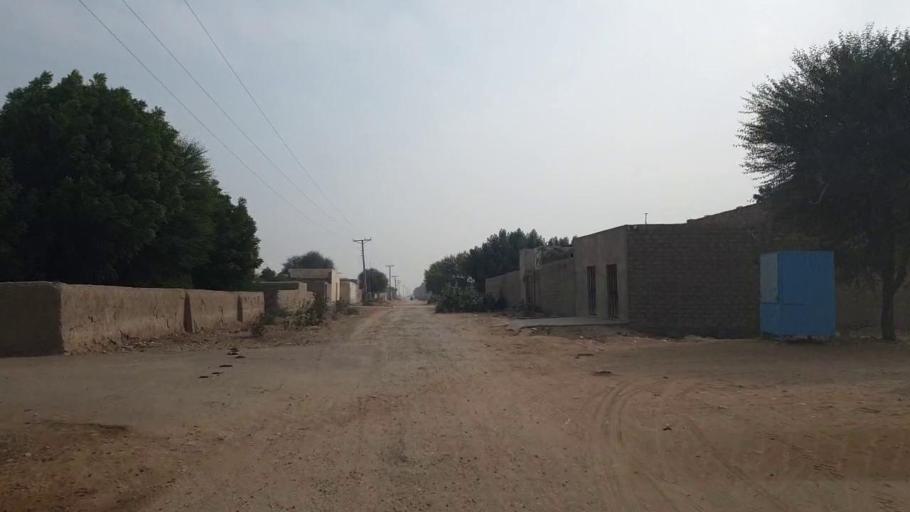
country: PK
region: Sindh
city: Sann
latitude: 26.0348
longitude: 68.1332
